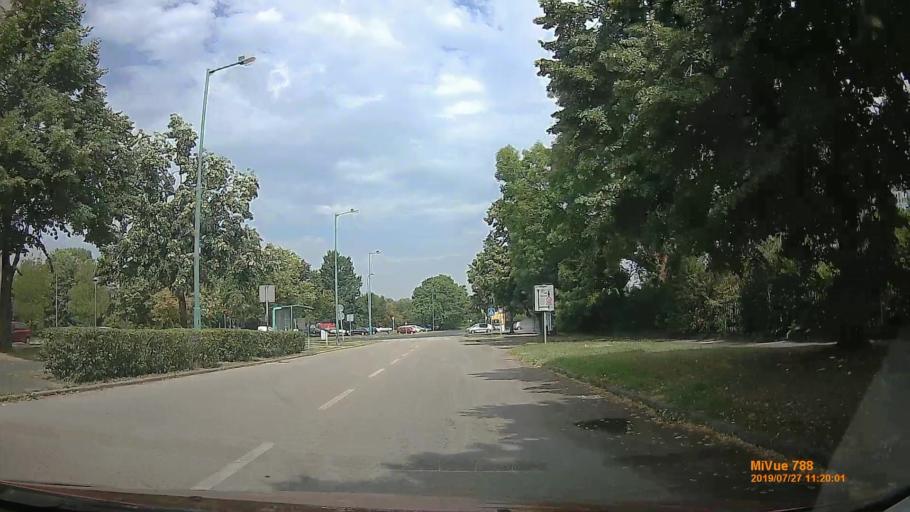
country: HU
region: Veszprem
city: Ajka
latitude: 47.1097
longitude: 17.5645
